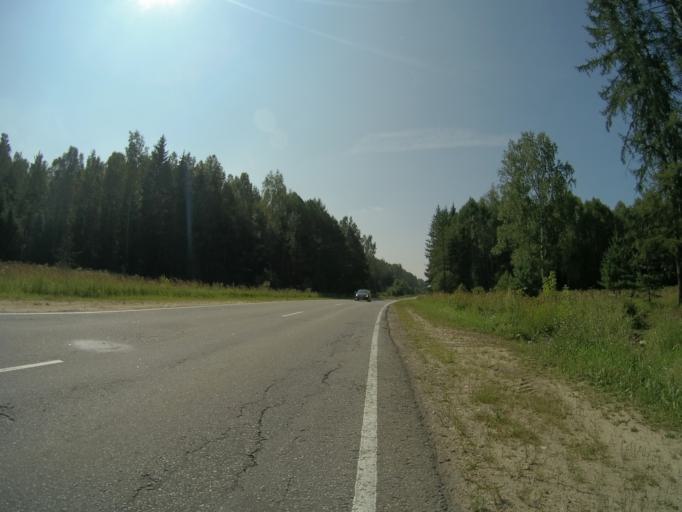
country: RU
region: Vladimir
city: Anopino
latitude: 55.7624
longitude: 40.6732
